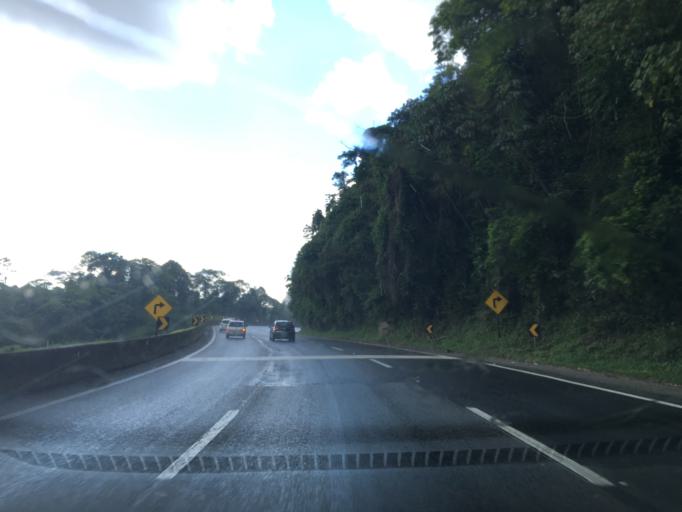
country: BR
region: Sao Paulo
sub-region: Mairipora
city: Mairipora
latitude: -23.3700
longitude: -46.5557
